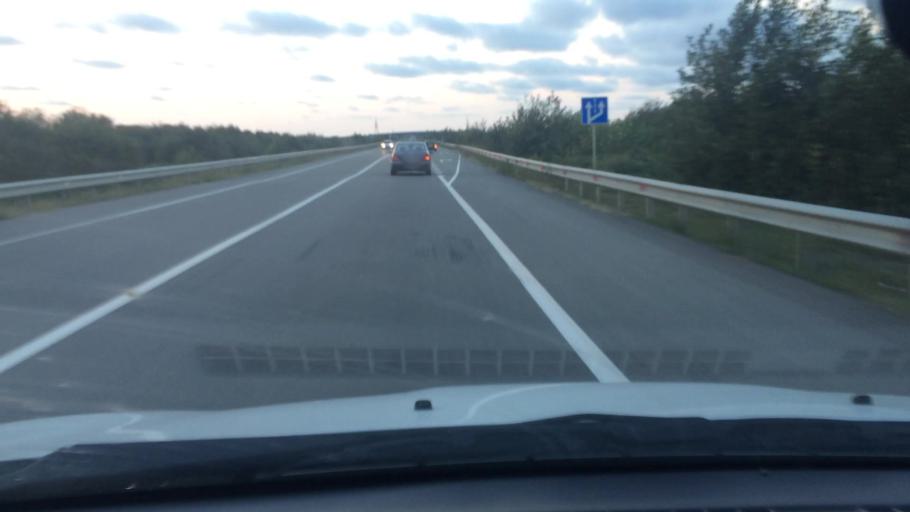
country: GE
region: Ajaria
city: Ochkhamuri
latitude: 41.8933
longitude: 41.8039
